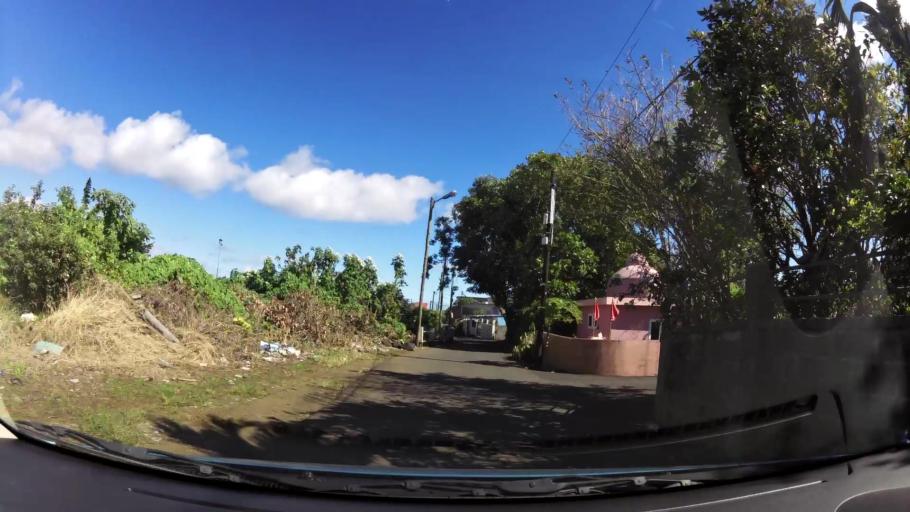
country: MU
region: Plaines Wilhems
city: Vacoas
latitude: -20.3271
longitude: 57.4843
